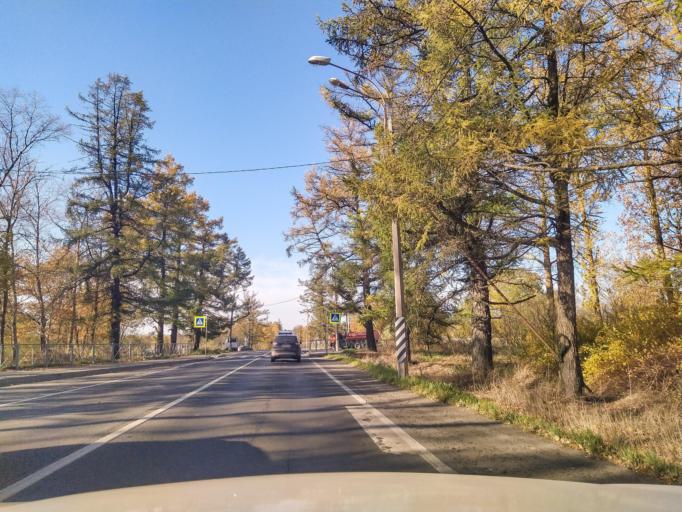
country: RU
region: St.-Petersburg
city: Aleksandrovskaya
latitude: 59.7073
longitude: 30.3331
